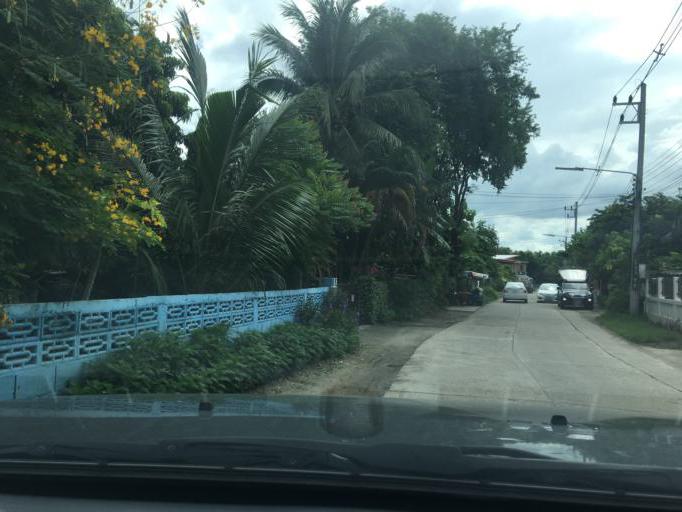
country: TH
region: Chiang Mai
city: San Sai
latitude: 18.8721
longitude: 98.9678
